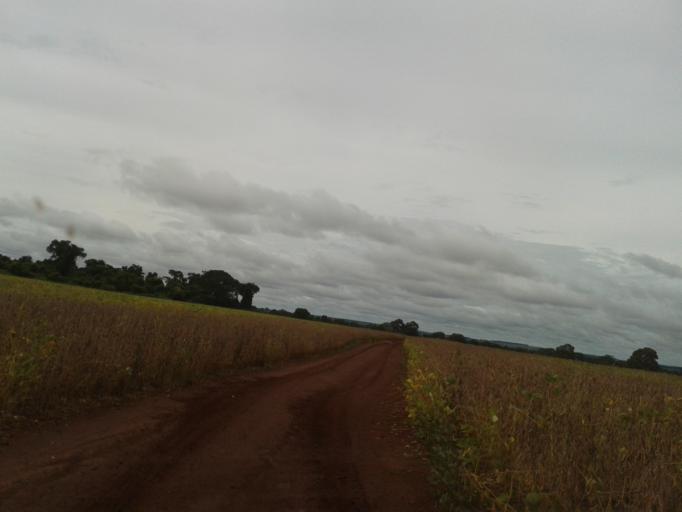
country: BR
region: Minas Gerais
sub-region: Capinopolis
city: Capinopolis
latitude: -18.7753
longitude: -49.7680
